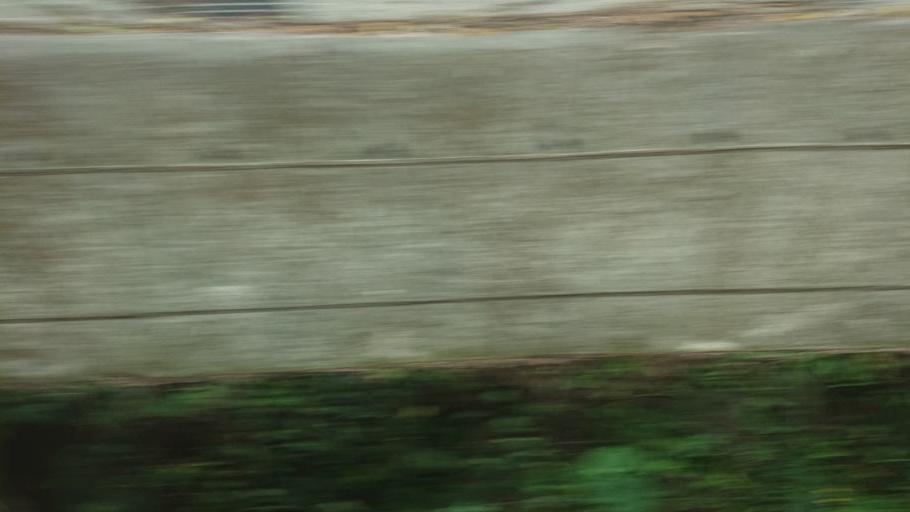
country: TW
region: Taiwan
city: Daxi
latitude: 24.8739
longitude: 121.3959
